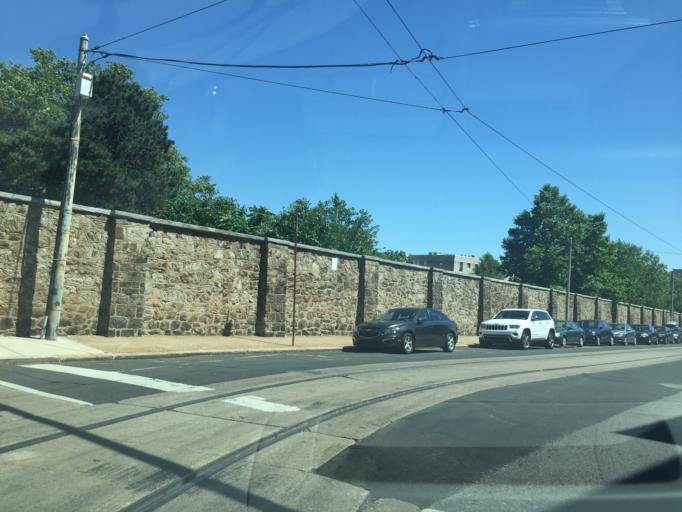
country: US
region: Pennsylvania
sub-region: Philadelphia County
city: Philadelphia
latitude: 39.9738
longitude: -75.1780
